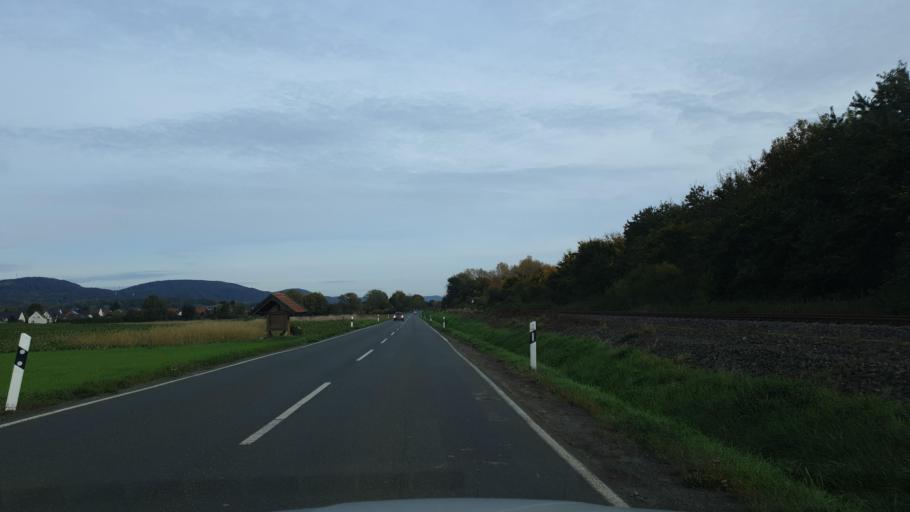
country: DE
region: North Rhine-Westphalia
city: Porta Westfalica
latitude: 52.1980
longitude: 8.9901
